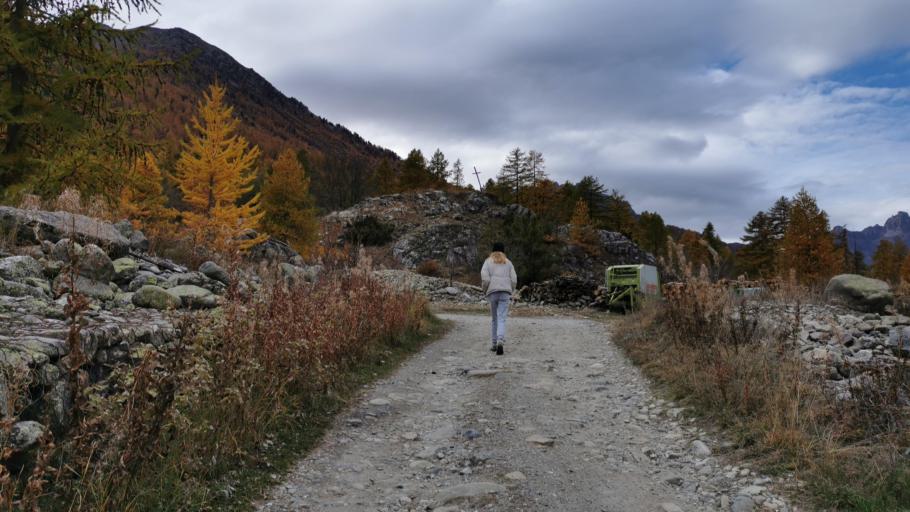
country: FR
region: Provence-Alpes-Cote d'Azur
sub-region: Departement des Hautes-Alpes
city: Villeneuve
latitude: 45.0173
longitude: 6.6045
